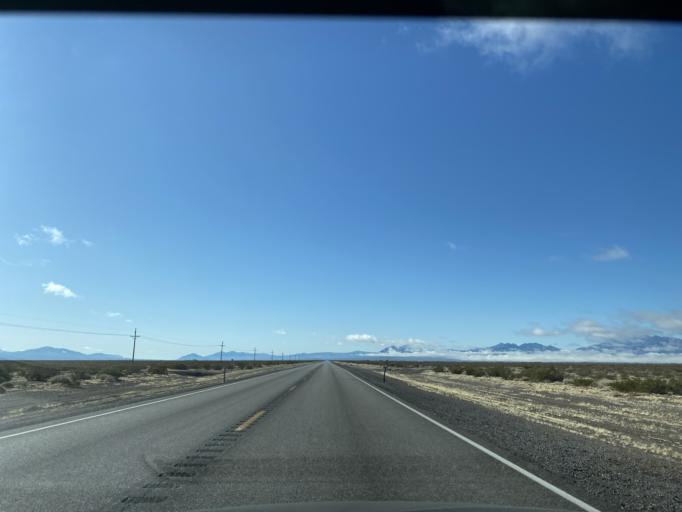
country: US
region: Nevada
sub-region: Nye County
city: Beatty
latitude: 36.6071
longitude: -116.4069
